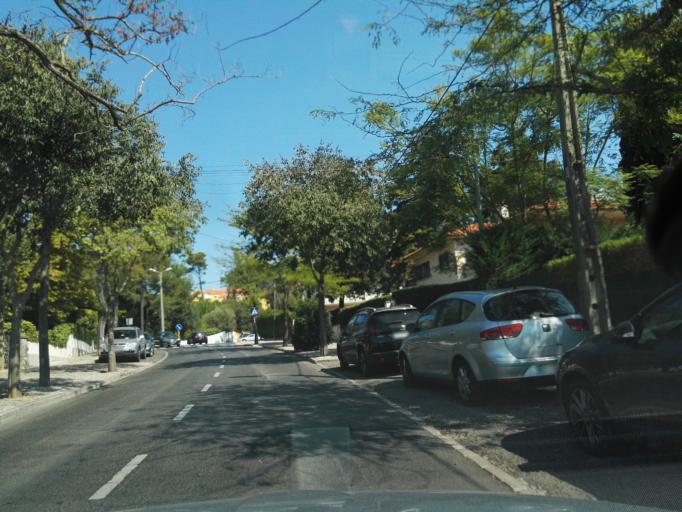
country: PT
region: Lisbon
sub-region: Cascais
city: Estoril
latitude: 38.7037
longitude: -9.3875
